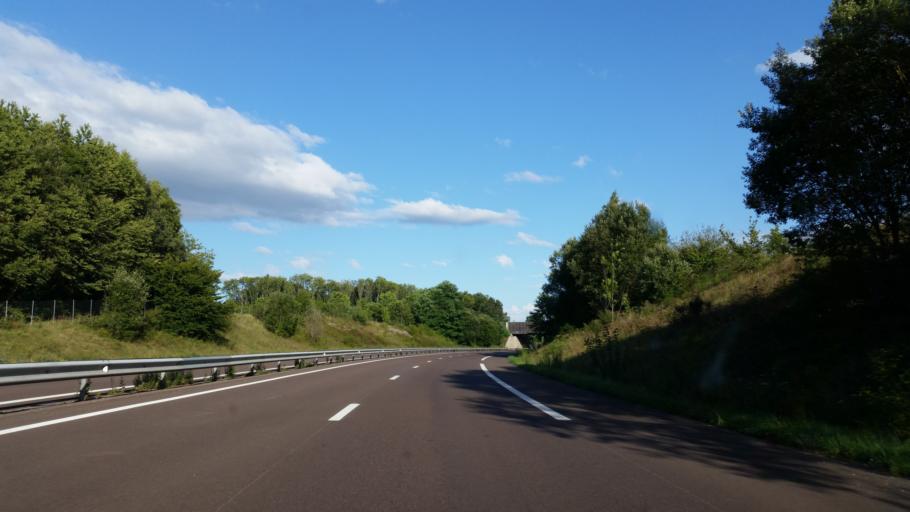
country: FR
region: Franche-Comte
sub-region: Departement de la Haute-Saone
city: Roye
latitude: 47.6656
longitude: 6.5612
